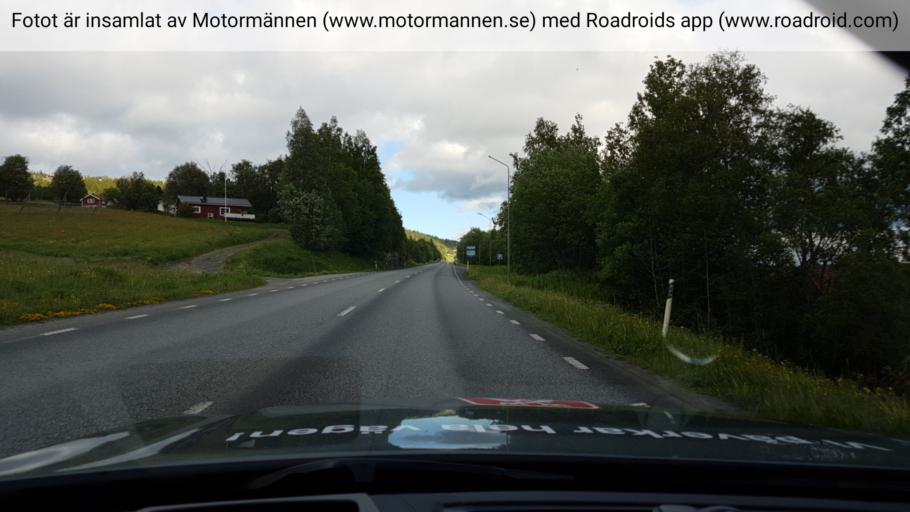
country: SE
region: Jaemtland
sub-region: Are Kommun
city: Are
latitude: 63.3844
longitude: 13.1317
